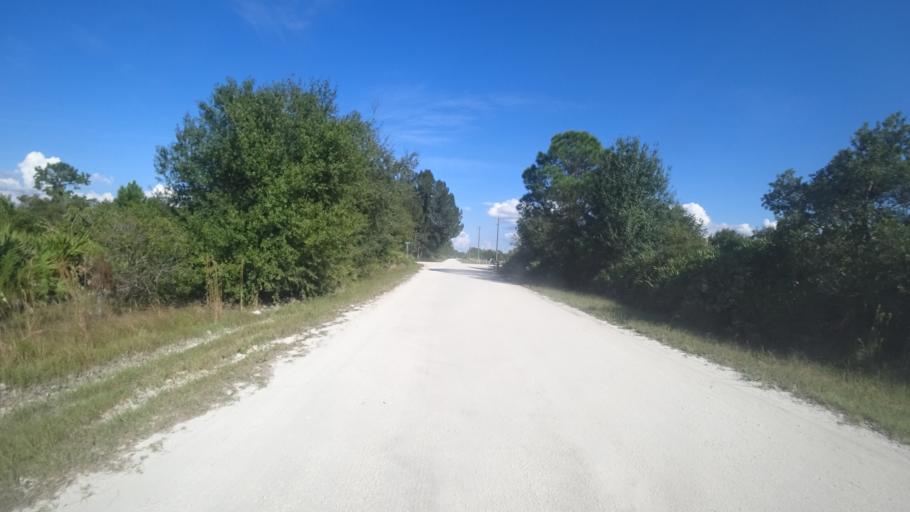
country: US
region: Florida
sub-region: Sarasota County
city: The Meadows
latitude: 27.4229
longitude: -82.2618
